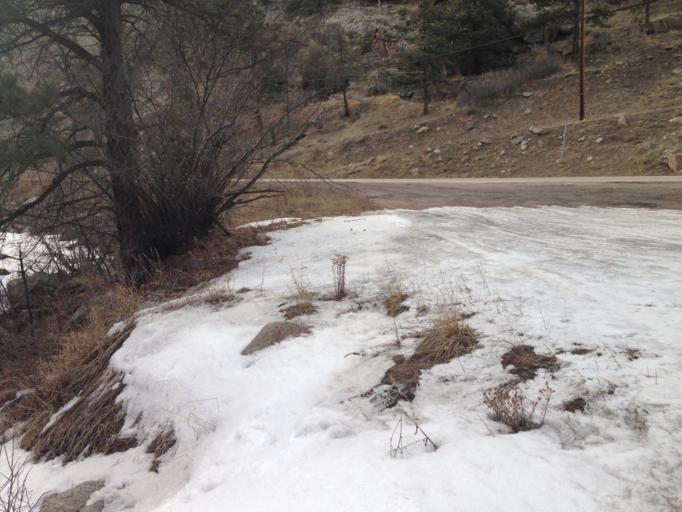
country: US
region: Colorado
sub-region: Boulder County
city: Coal Creek
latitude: 40.0032
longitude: -105.3674
